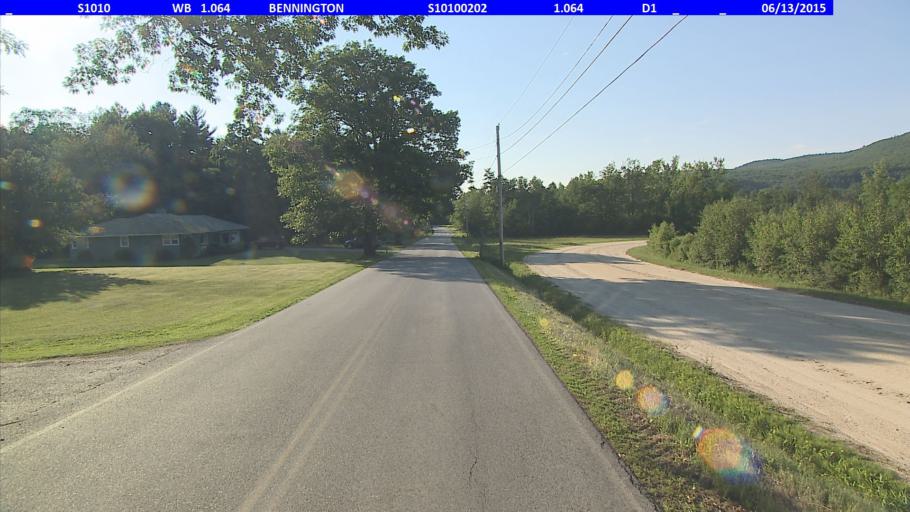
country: US
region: Vermont
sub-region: Bennington County
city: Bennington
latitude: 42.8742
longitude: -73.1566
